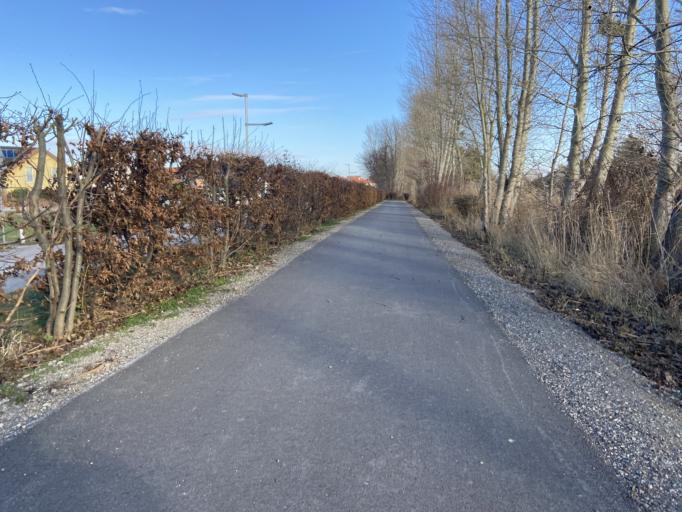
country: AT
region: Lower Austria
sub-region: Politischer Bezirk Modling
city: Neu-Guntramsdorf
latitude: 48.0570
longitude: 16.3171
